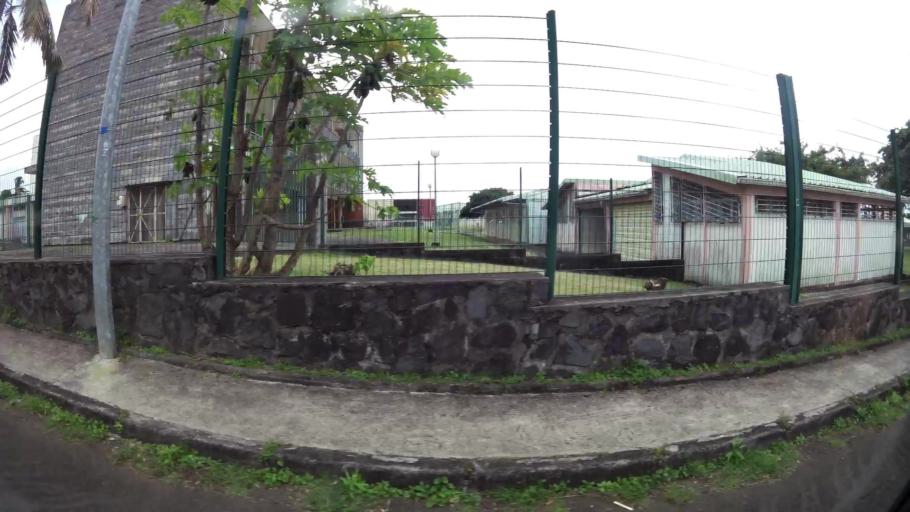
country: RE
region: Reunion
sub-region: Reunion
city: Sainte-Suzanne
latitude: -20.9014
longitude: 55.5996
